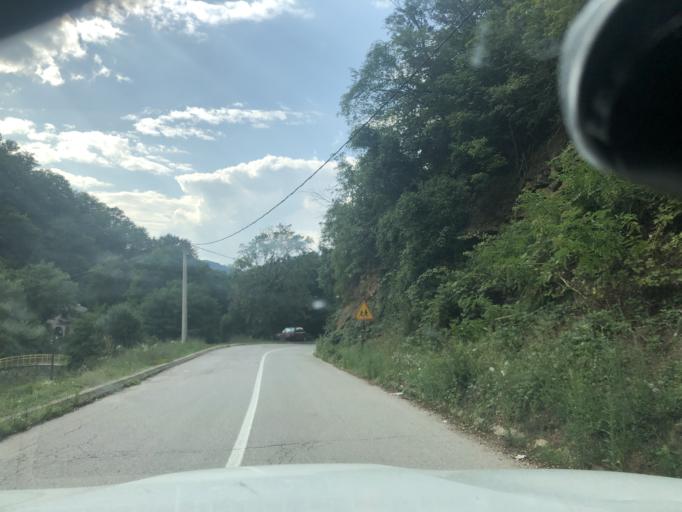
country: RS
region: Central Serbia
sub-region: Jablanicki Okrug
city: Medvega
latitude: 42.7780
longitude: 21.6005
